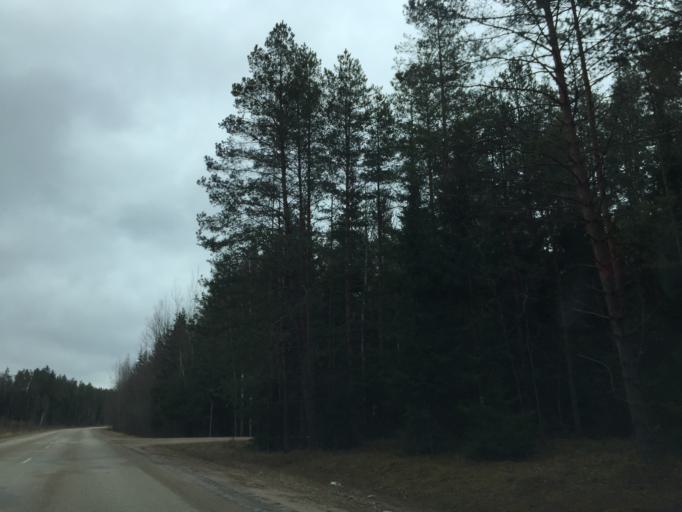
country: LV
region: Ilukste
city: Ilukste
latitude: 55.9529
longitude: 26.2962
